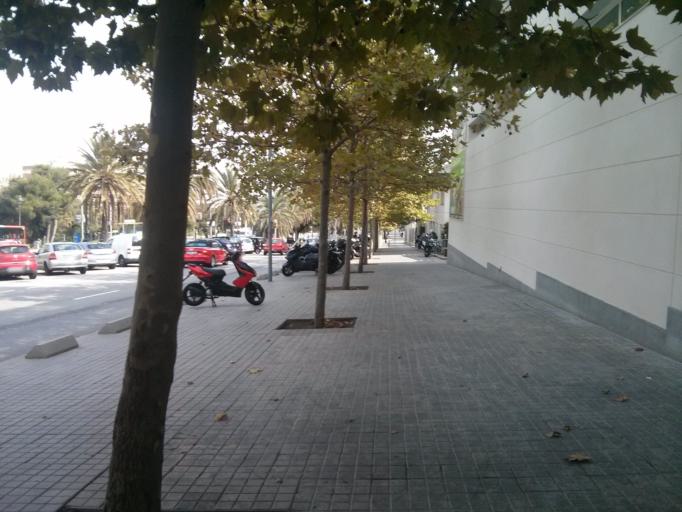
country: ES
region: Catalonia
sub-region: Provincia de Barcelona
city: Esplugues de Llobregat
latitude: 41.3828
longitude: 2.1074
